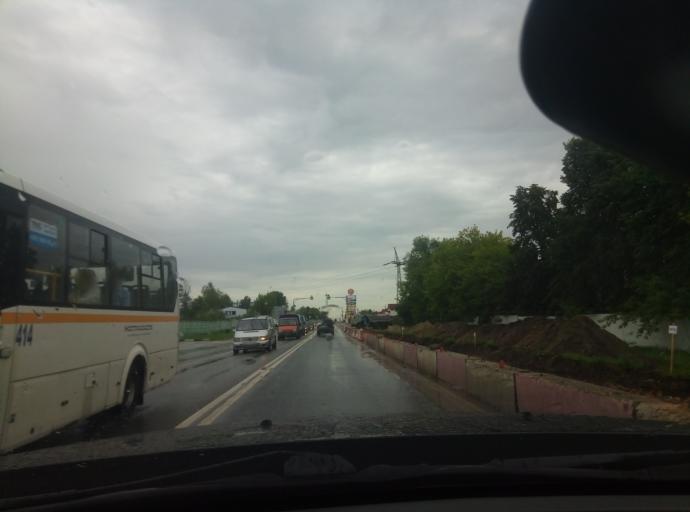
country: RU
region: Moskovskaya
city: Serpukhov
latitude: 54.9131
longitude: 37.4575
